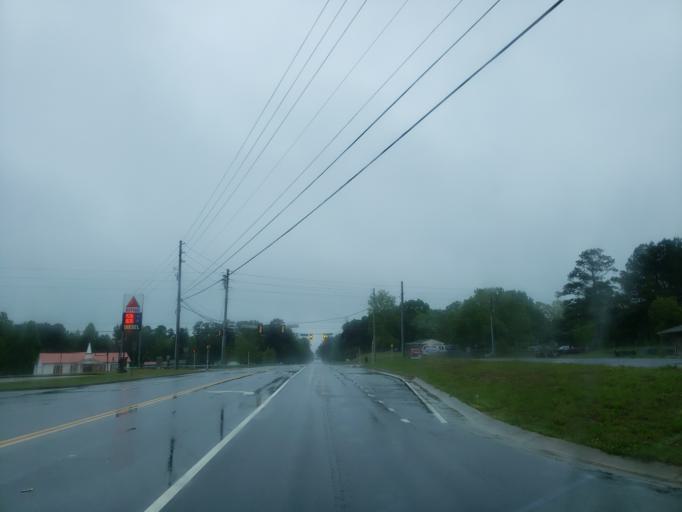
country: US
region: Georgia
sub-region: Carroll County
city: Villa Rica
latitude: 33.8209
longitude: -84.8799
